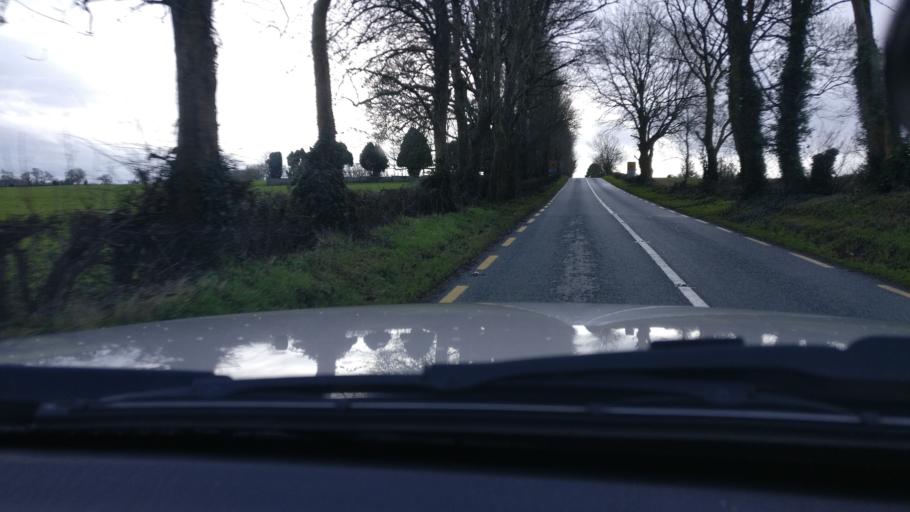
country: IE
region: Leinster
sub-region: An Iarmhi
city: Moate
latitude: 53.6061
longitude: -7.7107
